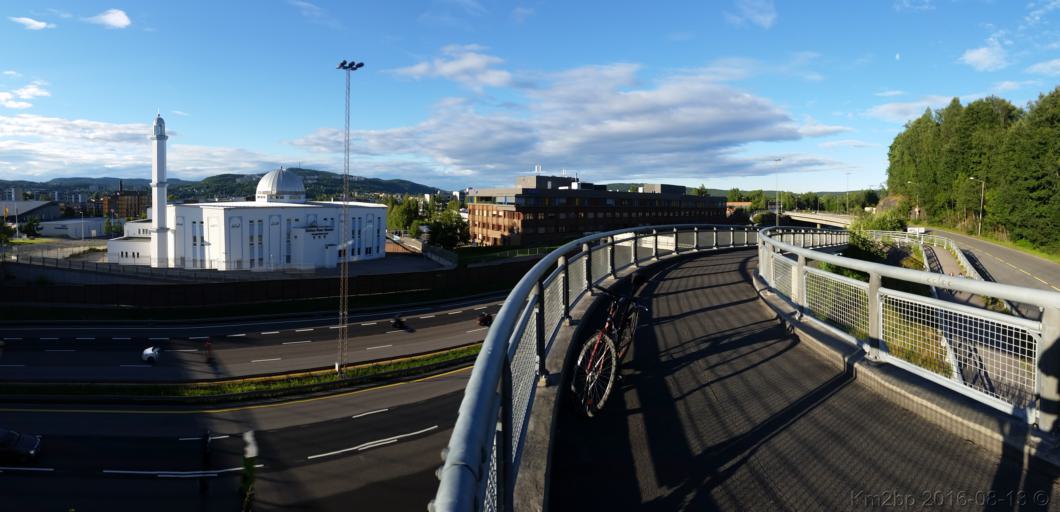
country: NO
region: Akershus
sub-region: Lorenskog
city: Kjenn
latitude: 59.9386
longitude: 10.8983
